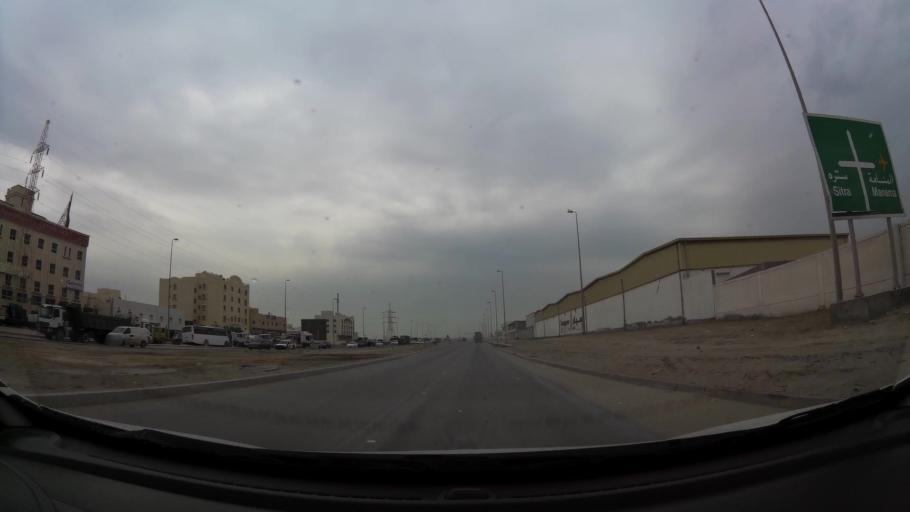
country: BH
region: Northern
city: Sitrah
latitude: 26.1750
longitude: 50.6034
